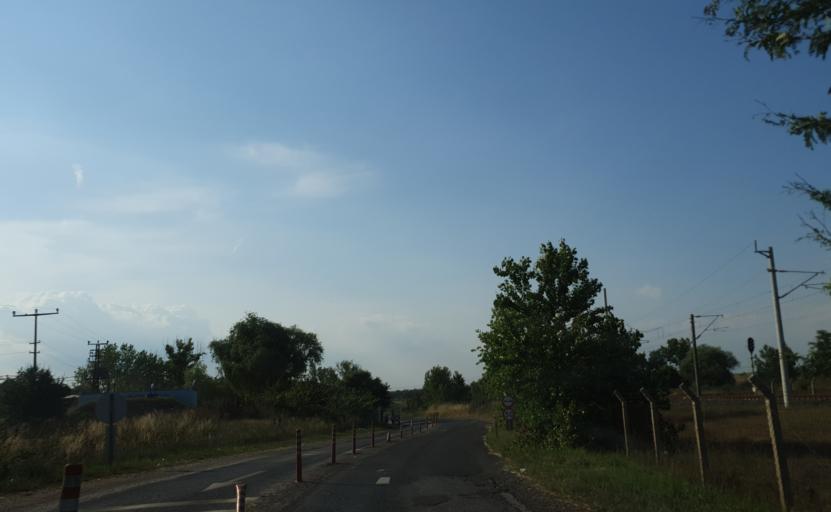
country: TR
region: Tekirdag
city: Muratli
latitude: 41.1833
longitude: 27.4817
